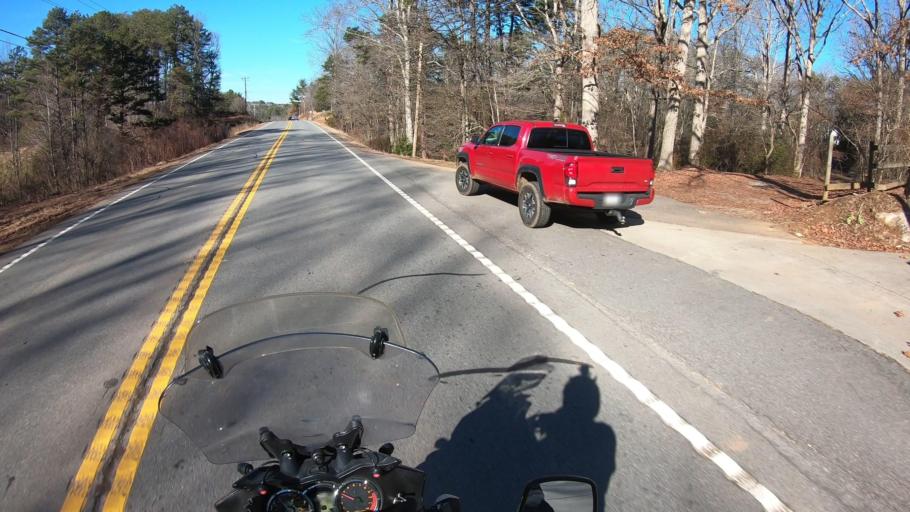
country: US
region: Georgia
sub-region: Fannin County
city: McCaysville
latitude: 34.9774
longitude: -84.3311
